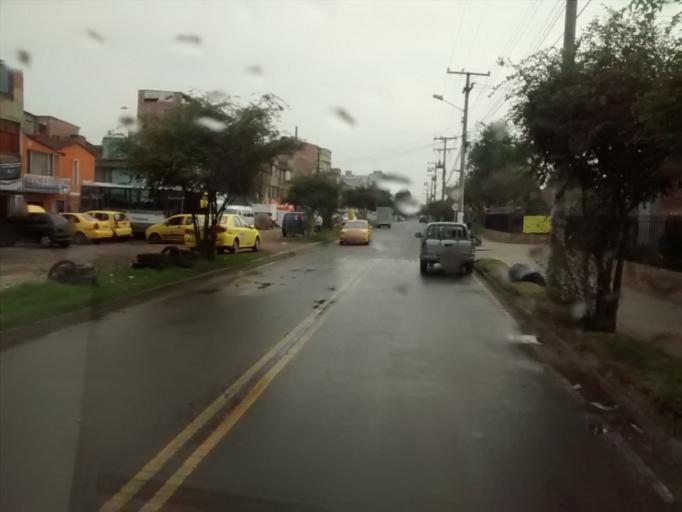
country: CO
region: Cundinamarca
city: Cota
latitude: 4.7571
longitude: -74.0964
